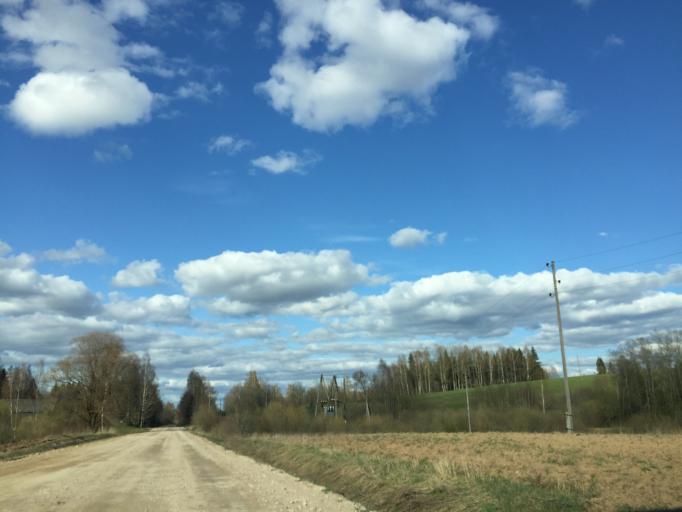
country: LV
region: Rezekne
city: Rezekne
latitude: 56.6330
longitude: 27.3085
